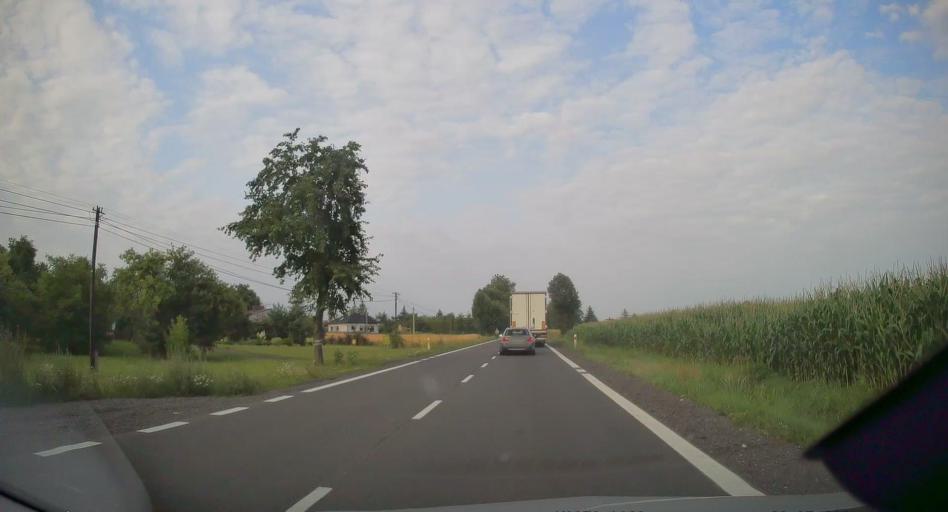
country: PL
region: Silesian Voivodeship
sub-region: Powiat czestochowski
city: Borowno
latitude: 50.9037
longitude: 19.2920
